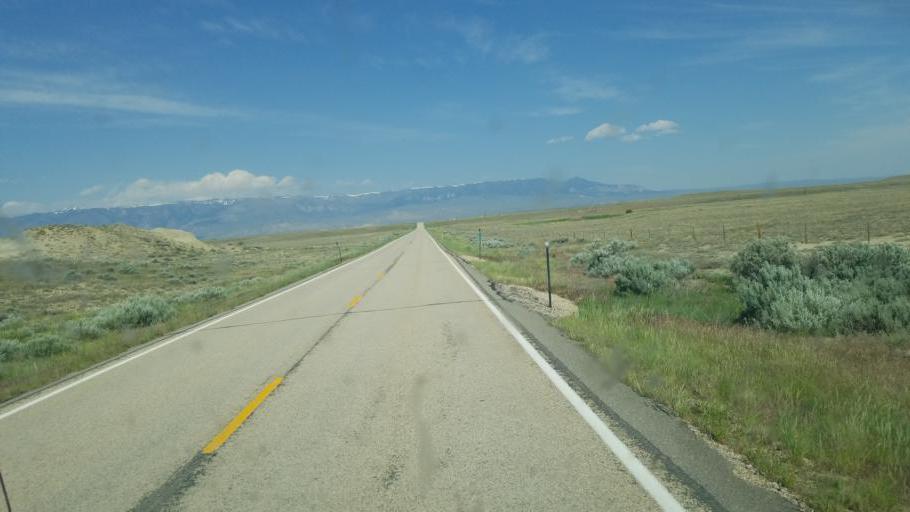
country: US
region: Wyoming
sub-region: Park County
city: Powell
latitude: 44.8506
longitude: -109.0095
